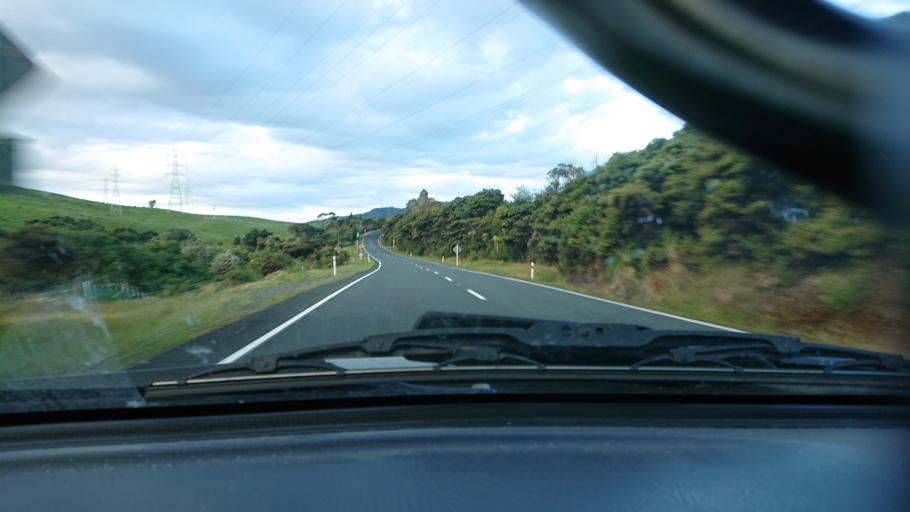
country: NZ
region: Auckland
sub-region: Auckland
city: Parakai
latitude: -36.4785
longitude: 174.4475
